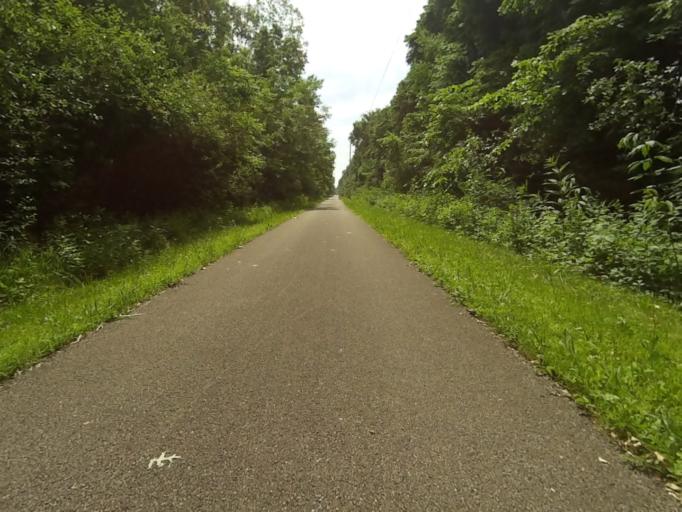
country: US
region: Ohio
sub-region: Summit County
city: Hudson
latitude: 41.2255
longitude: -81.4835
